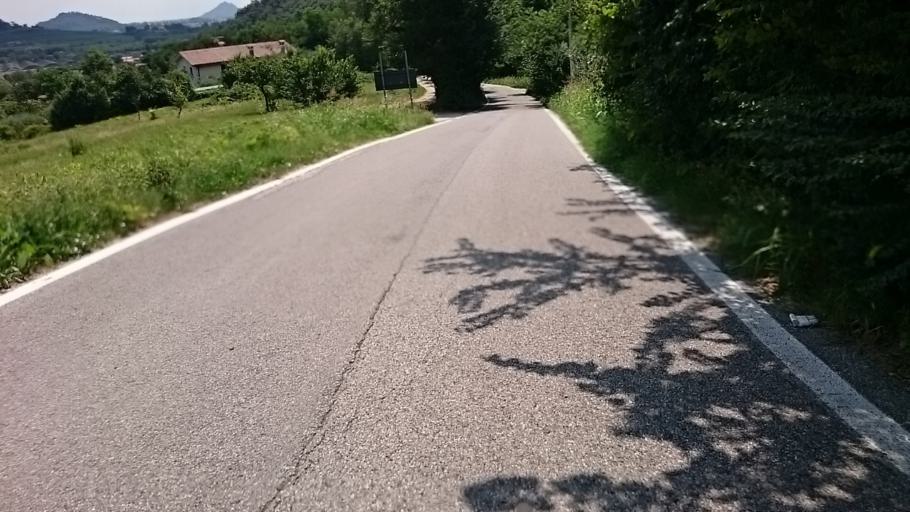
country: IT
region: Veneto
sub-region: Provincia di Padova
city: Galzignano
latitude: 45.3163
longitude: 11.7557
